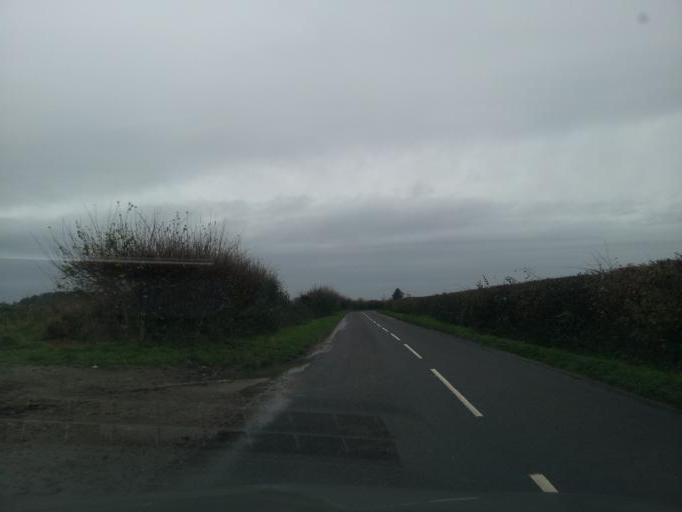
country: GB
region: England
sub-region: Essex
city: West Bergholt
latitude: 51.9380
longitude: 0.8208
